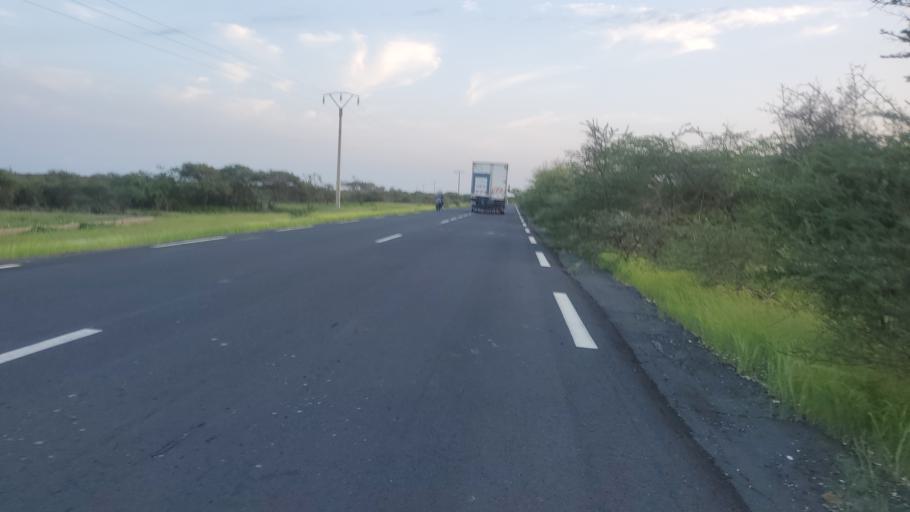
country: SN
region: Saint-Louis
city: Saint-Louis
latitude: 16.1239
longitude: -16.4138
